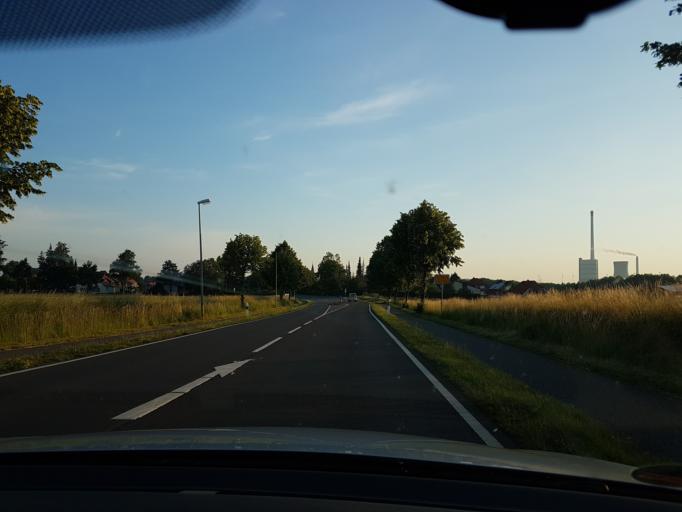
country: DE
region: Lower Saxony
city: Schoningen
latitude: 52.1530
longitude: 10.9660
